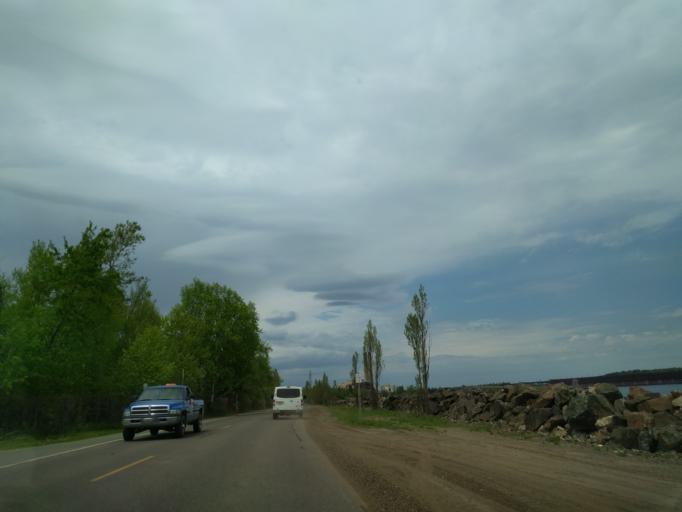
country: US
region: Michigan
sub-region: Marquette County
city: Marquette
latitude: 46.5664
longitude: -87.3912
